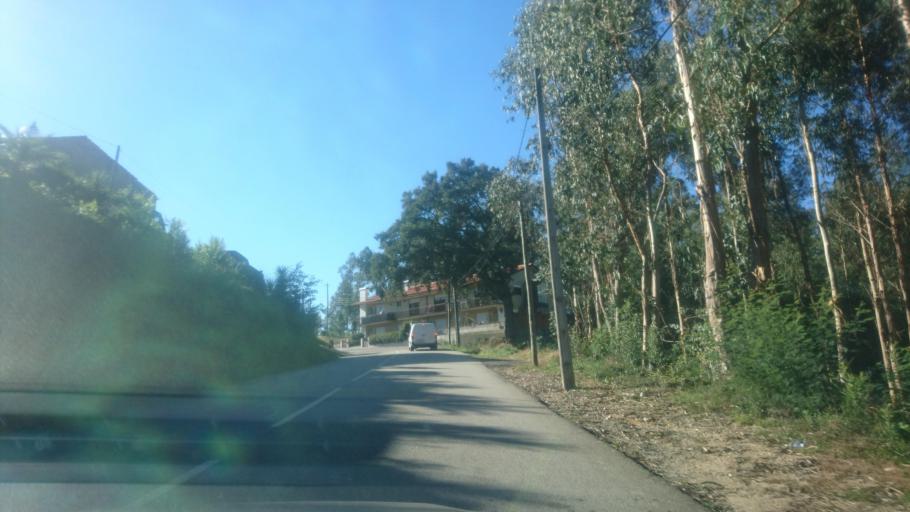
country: PT
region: Aveiro
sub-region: Oliveira de Azemeis
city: Vila Cha
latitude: 40.8634
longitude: -8.4392
